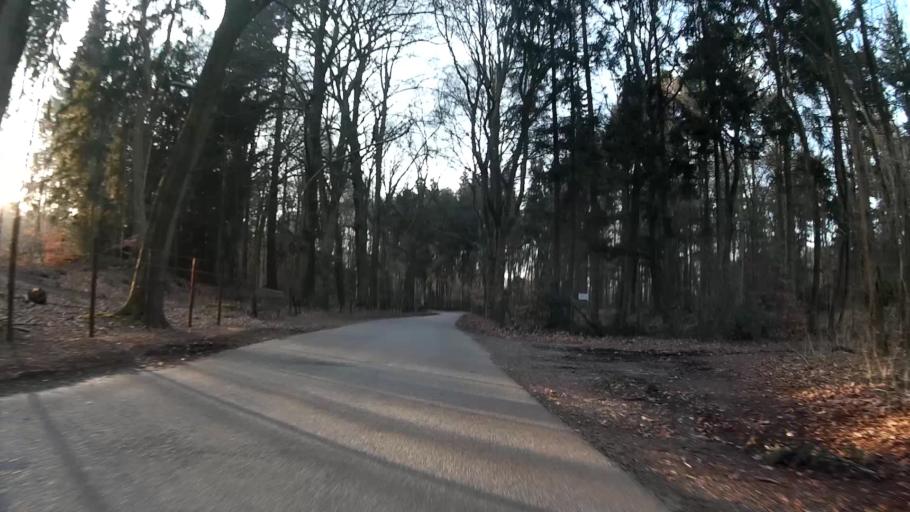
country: NL
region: Utrecht
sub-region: Gemeente Veenendaal
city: Veenendaal
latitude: 52.0076
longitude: 5.5347
